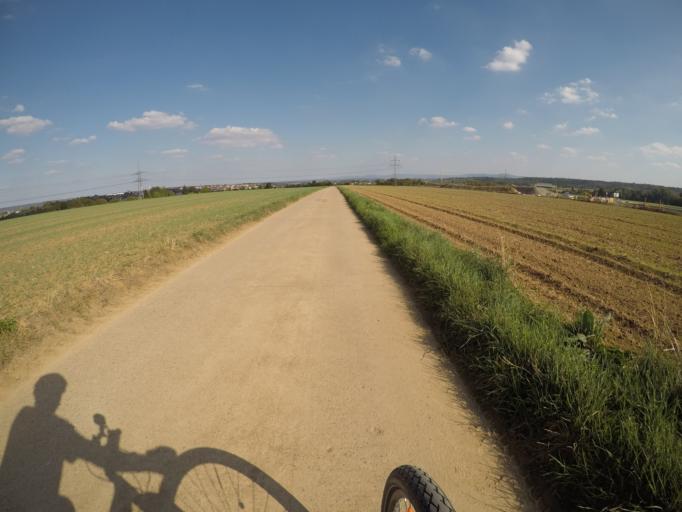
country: DE
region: Baden-Wuerttemberg
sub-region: Regierungsbezirk Stuttgart
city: Neuhausen auf den Fildern
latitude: 48.6954
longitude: 9.2943
